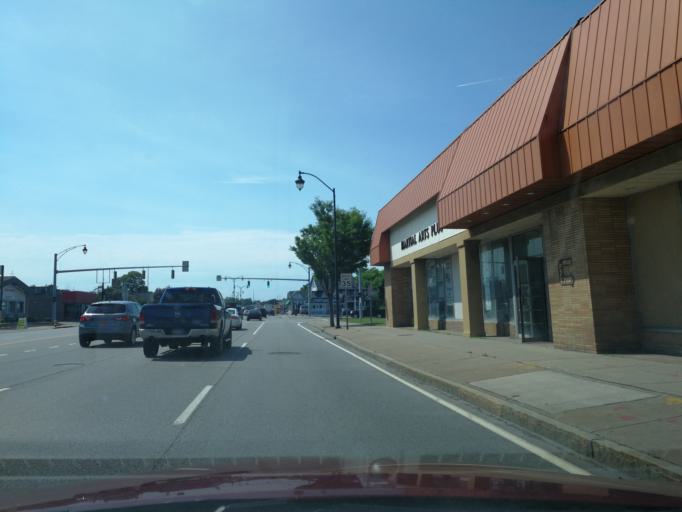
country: US
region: New York
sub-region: Monroe County
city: Rochester
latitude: 43.2011
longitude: -77.6395
